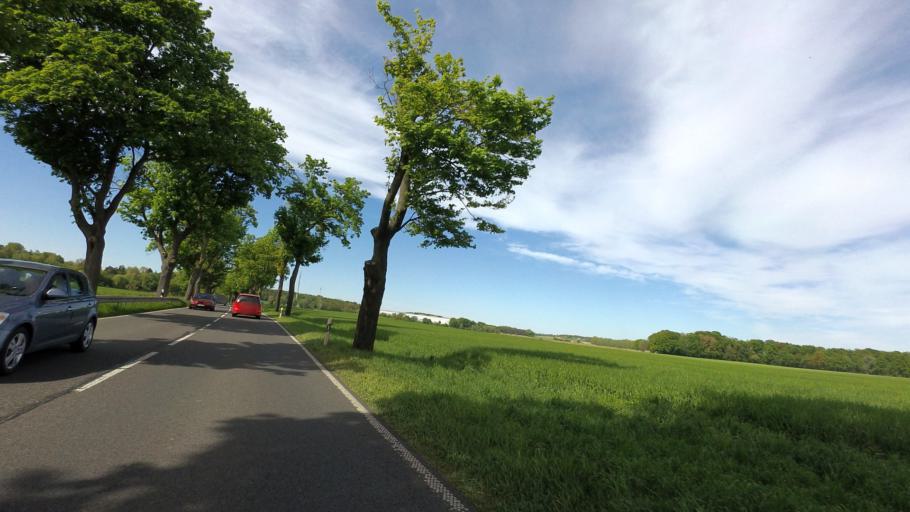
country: DE
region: Brandenburg
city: Rangsdorf
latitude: 52.2847
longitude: 13.4626
